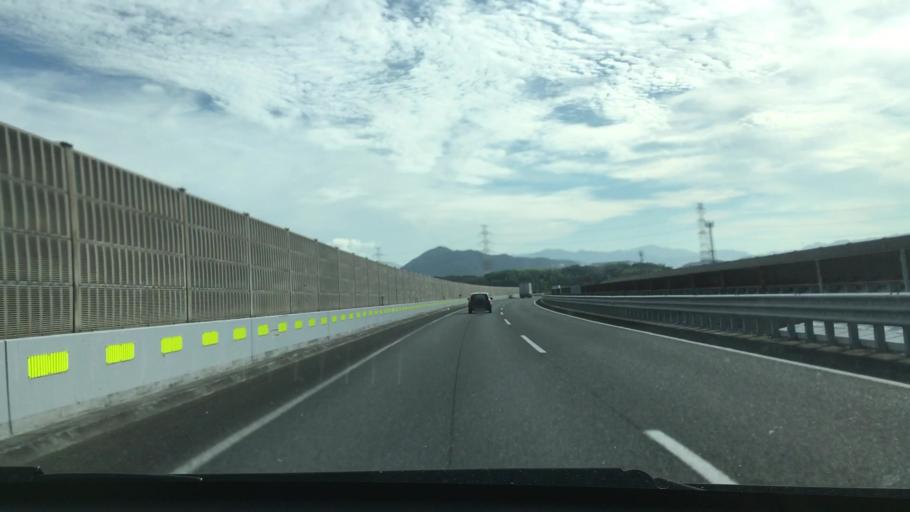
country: JP
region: Fukuoka
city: Kanda
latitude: 33.8359
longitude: 130.9228
